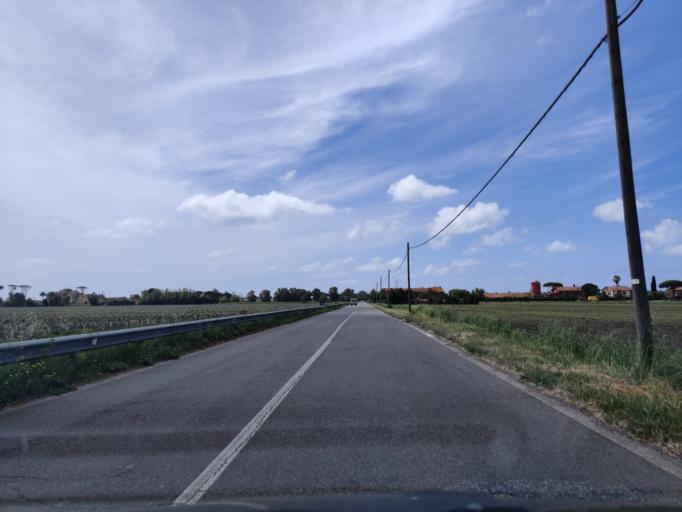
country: IT
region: Latium
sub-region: Citta metropolitana di Roma Capitale
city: Maccarese
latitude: 41.8831
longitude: 12.2193
